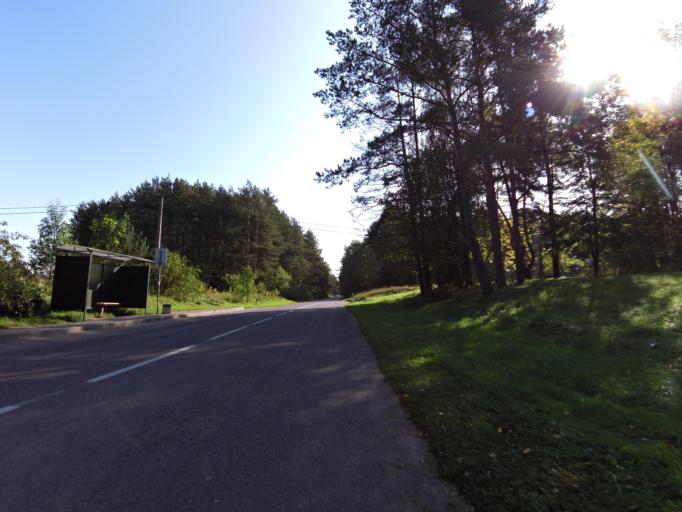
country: LT
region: Vilnius County
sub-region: Vilnius
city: Vilnius
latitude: 54.7435
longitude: 25.3032
